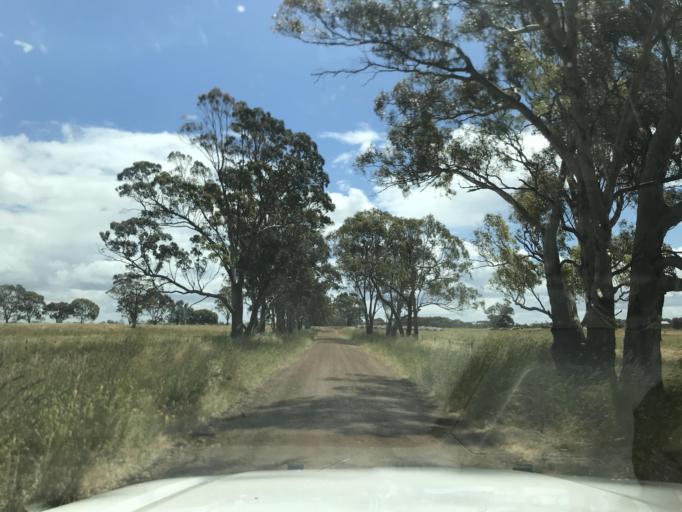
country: AU
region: South Australia
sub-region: Wattle Range
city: Penola
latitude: -37.1241
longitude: 141.2877
